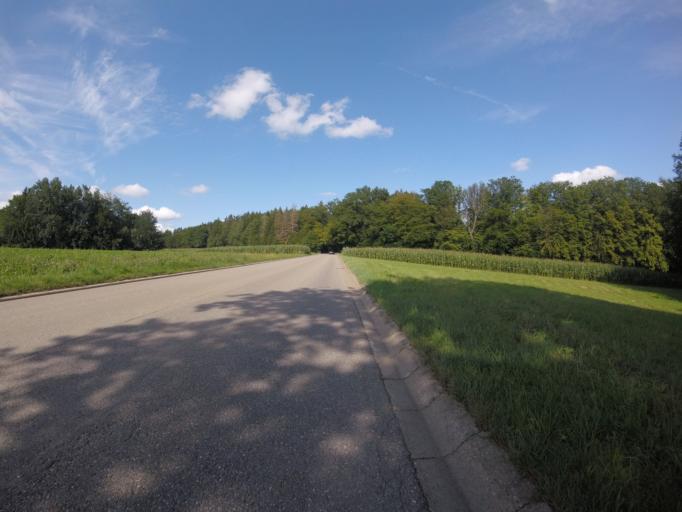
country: DE
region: Baden-Wuerttemberg
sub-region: Regierungsbezirk Stuttgart
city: Oppenweiler
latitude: 48.9638
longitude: 9.4702
